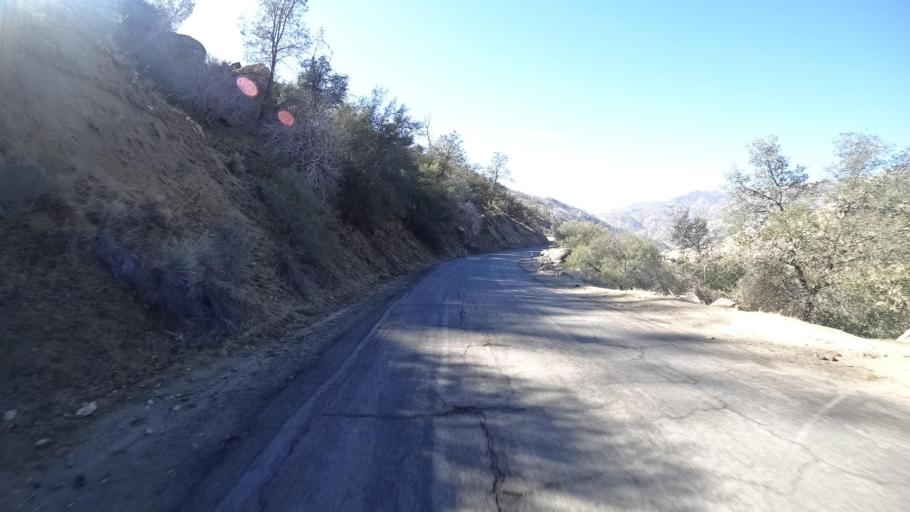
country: US
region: California
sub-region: Kern County
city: Bodfish
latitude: 35.5539
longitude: -118.5813
